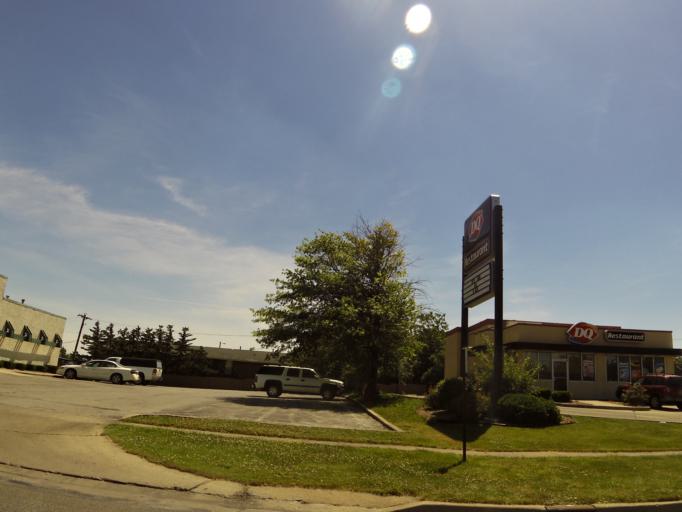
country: US
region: Illinois
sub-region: Vermilion County
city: Danville
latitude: 40.1682
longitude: -87.6306
